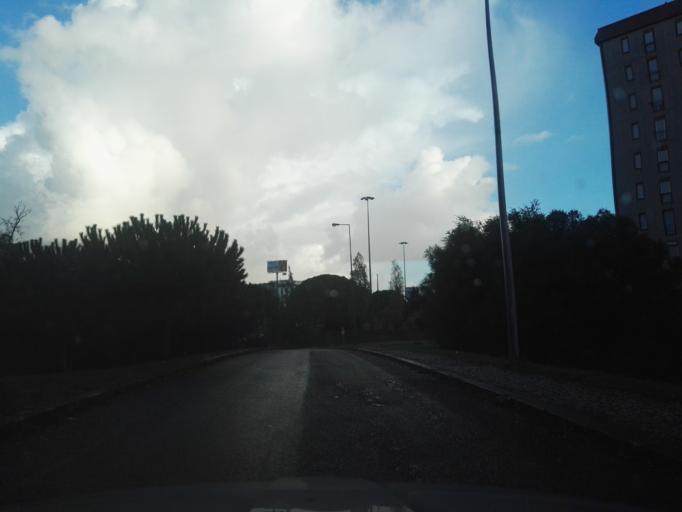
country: PT
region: Lisbon
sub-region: Loures
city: Sacavem
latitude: 38.7811
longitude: -9.1223
